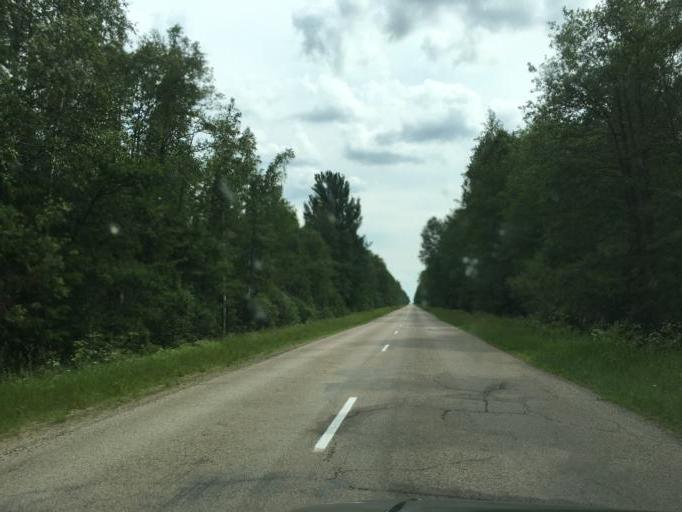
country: LV
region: Rugaju
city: Rugaji
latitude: 56.7974
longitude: 27.0991
